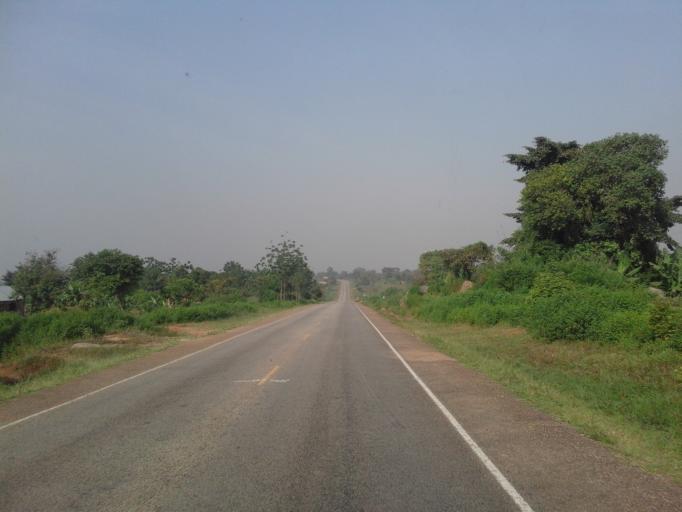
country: UG
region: Eastern Region
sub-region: Budaka District
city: Budaka
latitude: 1.0387
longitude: 34.0123
